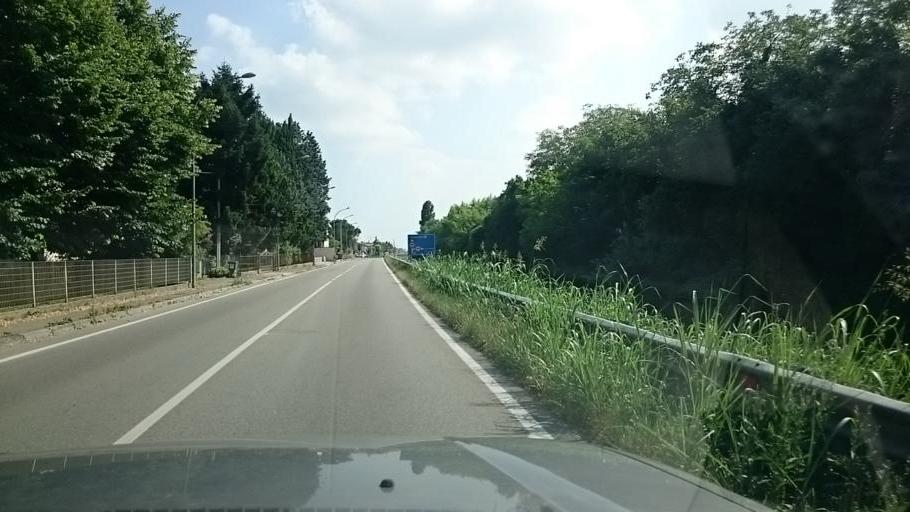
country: IT
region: Veneto
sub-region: Provincia di Padova
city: San Giorgio delle Pertiche
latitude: 45.5437
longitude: 11.8753
